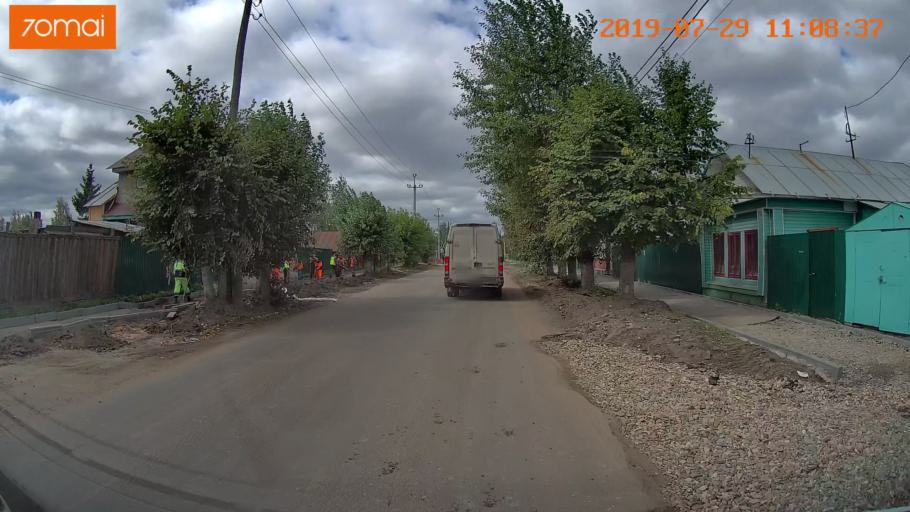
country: RU
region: Ivanovo
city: Bogorodskoye
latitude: 56.9954
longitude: 41.0341
